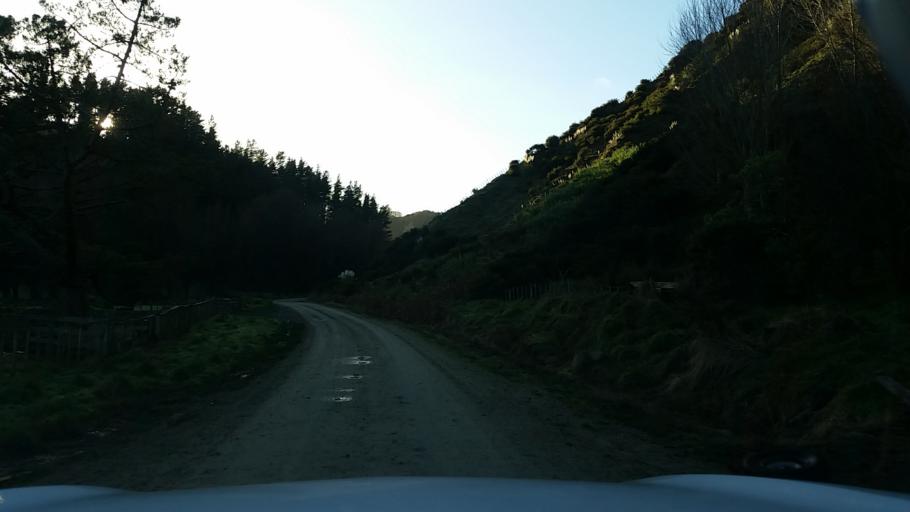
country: NZ
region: Taranaki
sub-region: South Taranaki District
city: Patea
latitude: -39.7600
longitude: 174.7295
